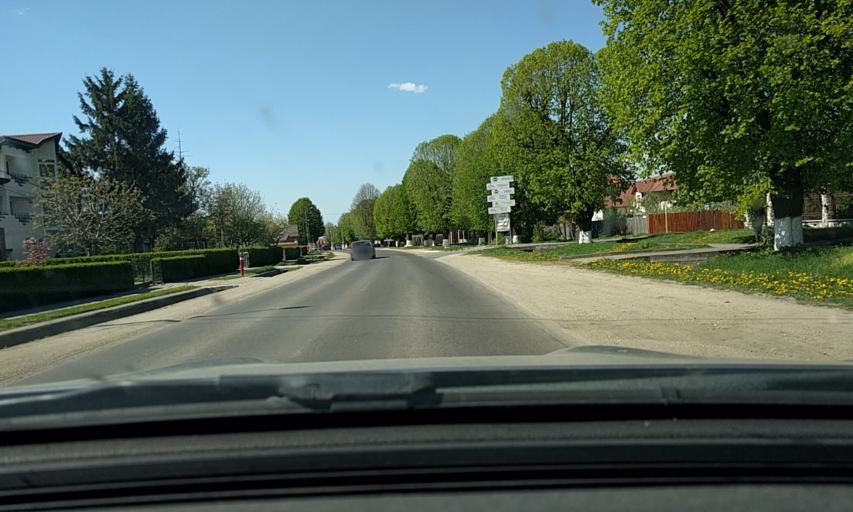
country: RO
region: Brasov
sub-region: Comuna Harman
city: Harman
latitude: 45.7074
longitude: 25.6870
